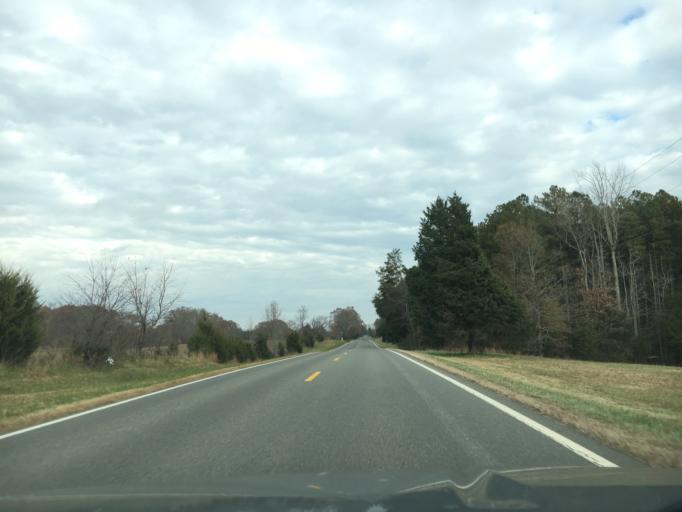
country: US
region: Virginia
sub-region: Cumberland County
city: Cumberland
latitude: 37.4490
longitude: -78.3186
